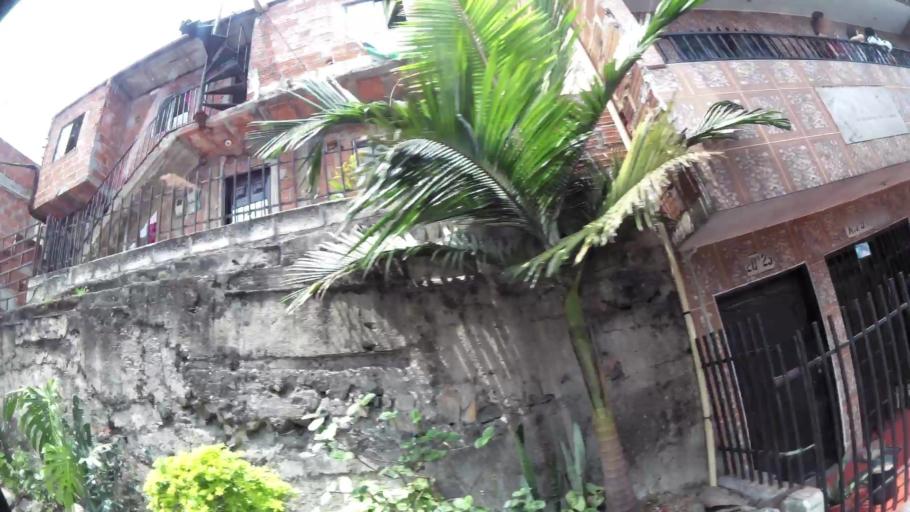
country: CO
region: Antioquia
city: Bello
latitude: 6.3149
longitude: -75.5841
